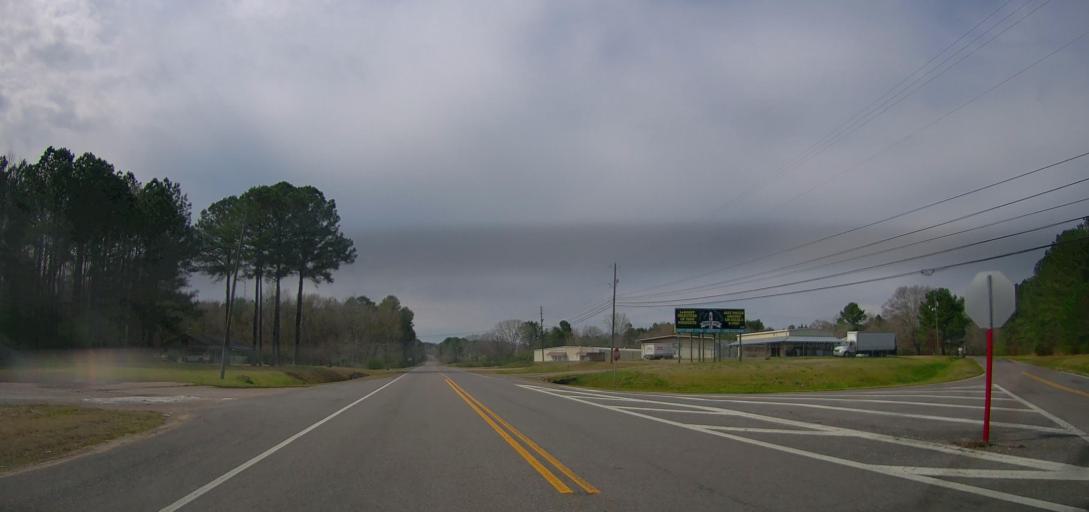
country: US
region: Alabama
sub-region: Walker County
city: Carbon Hill
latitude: 33.9055
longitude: -87.5521
